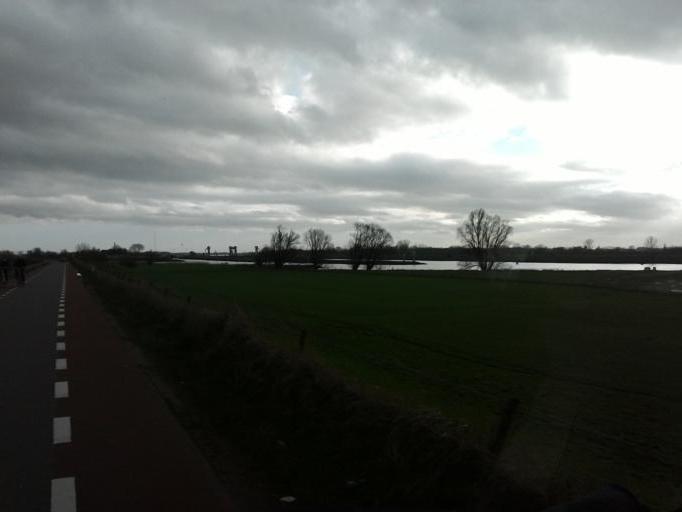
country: NL
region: Utrecht
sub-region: Gemeente Vianen
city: Vianen
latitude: 52.0020
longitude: 5.1243
